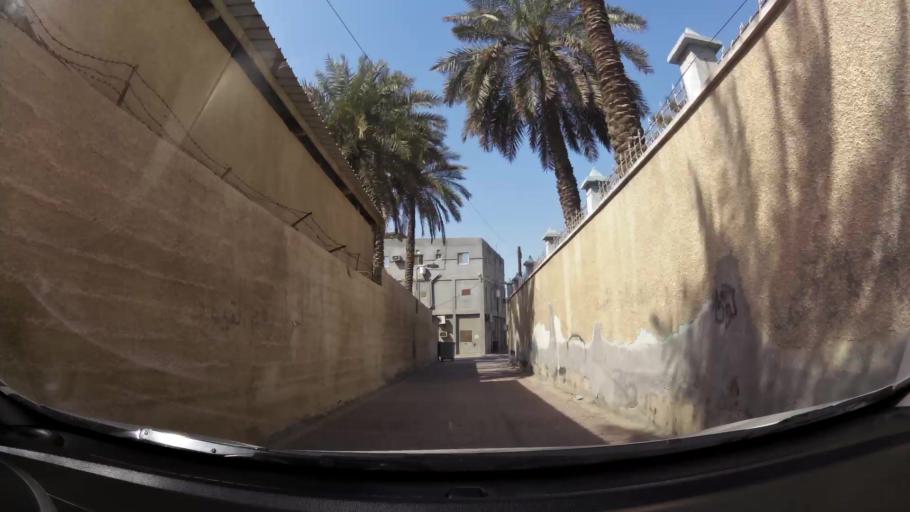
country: BH
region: Manama
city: Jidd Hafs
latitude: 26.2088
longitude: 50.4597
